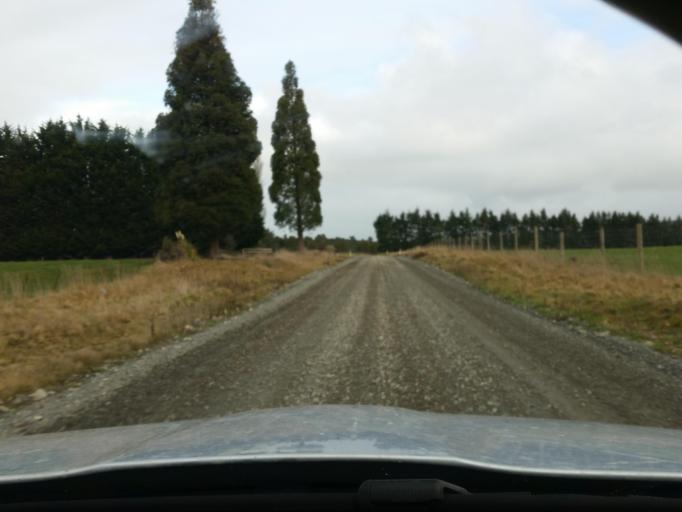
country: NZ
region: Southland
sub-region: Southland District
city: Riverton
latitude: -45.9400
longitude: 167.7049
